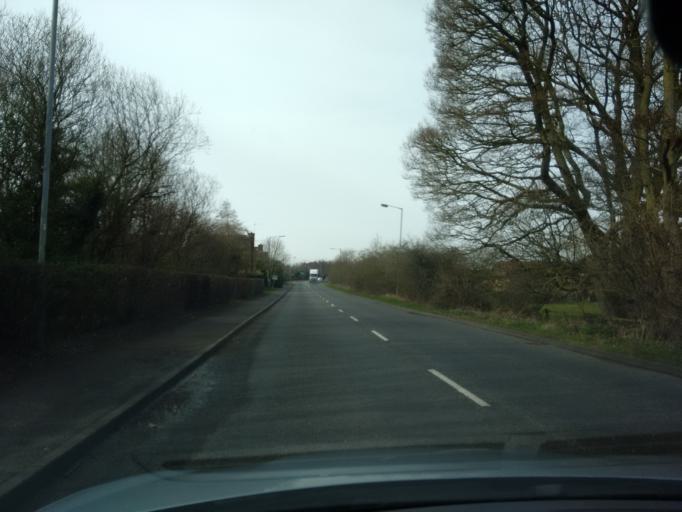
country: GB
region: England
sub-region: Warwickshire
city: Alcester
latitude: 52.2247
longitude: -1.8756
